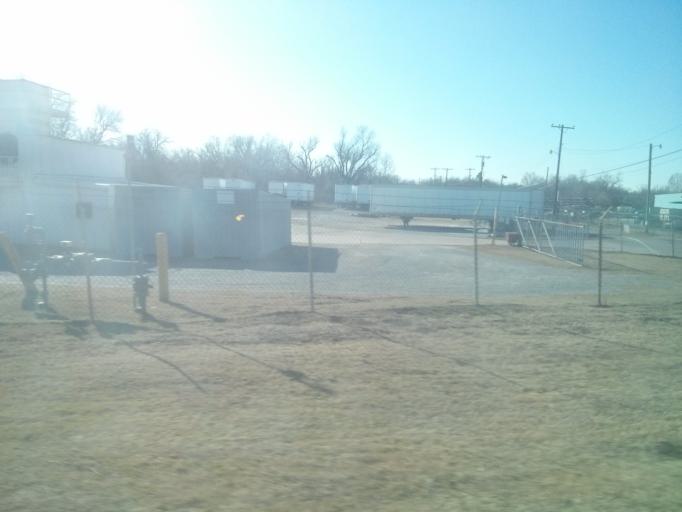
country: US
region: Oklahoma
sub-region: Tulsa County
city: Tulsa
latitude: 36.1770
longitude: -95.9326
